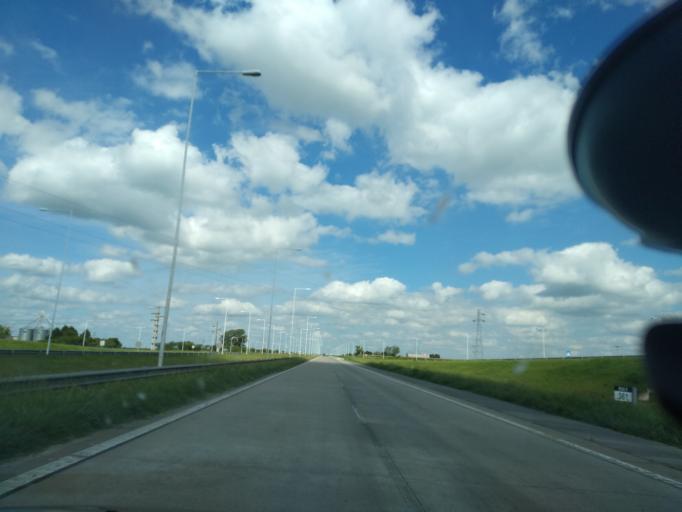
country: AR
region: Santa Fe
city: Canada de Gomez
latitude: -32.8468
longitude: -61.3905
